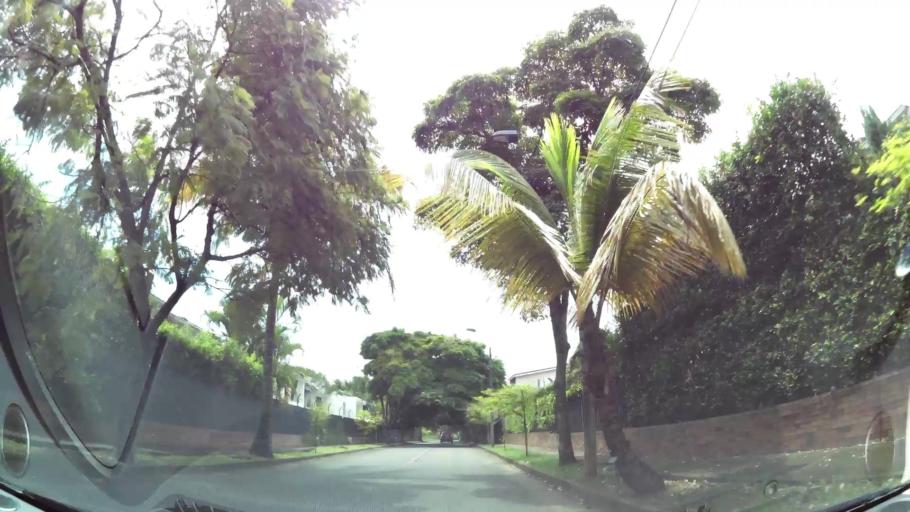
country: CO
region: Valle del Cauca
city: Cali
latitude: 3.3861
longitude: -76.5356
